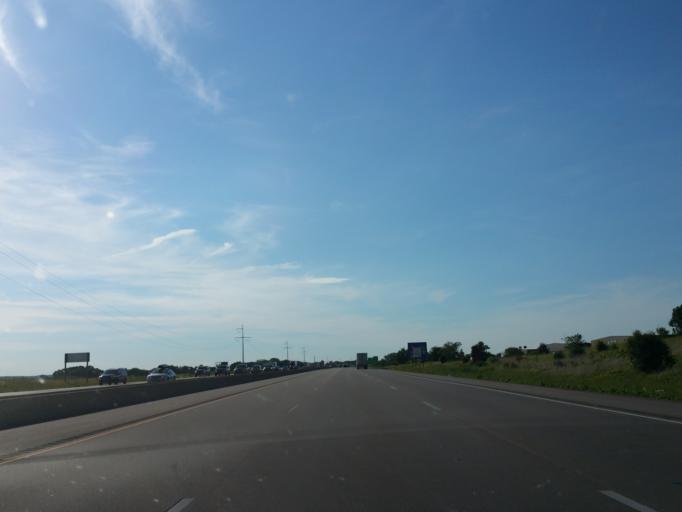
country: US
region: Wisconsin
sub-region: Dane County
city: Windsor
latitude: 43.1862
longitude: -89.3339
